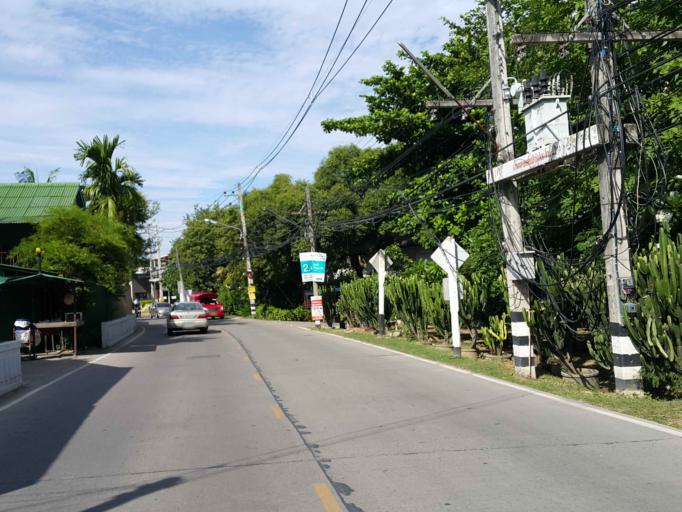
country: TH
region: Chiang Mai
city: Chiang Mai
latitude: 18.7585
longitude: 98.9954
